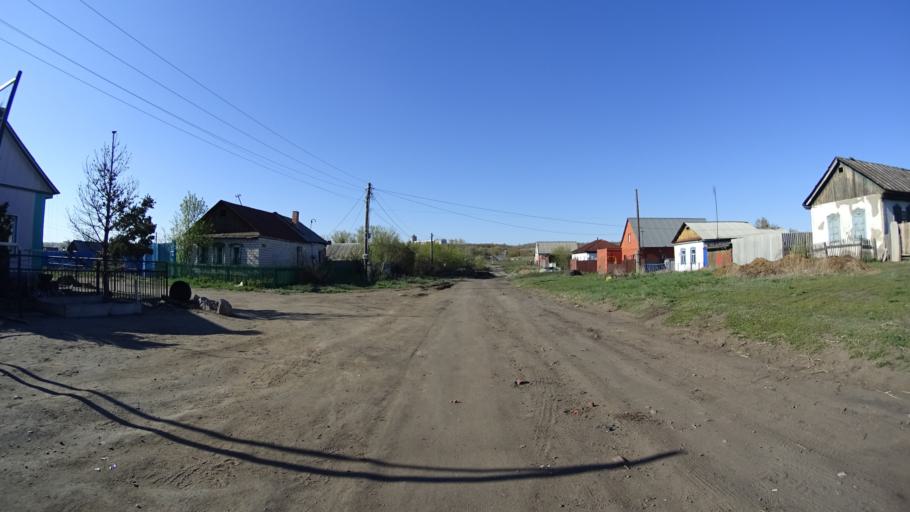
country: RU
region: Chelyabinsk
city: Troitsk
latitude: 54.0927
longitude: 61.5998
